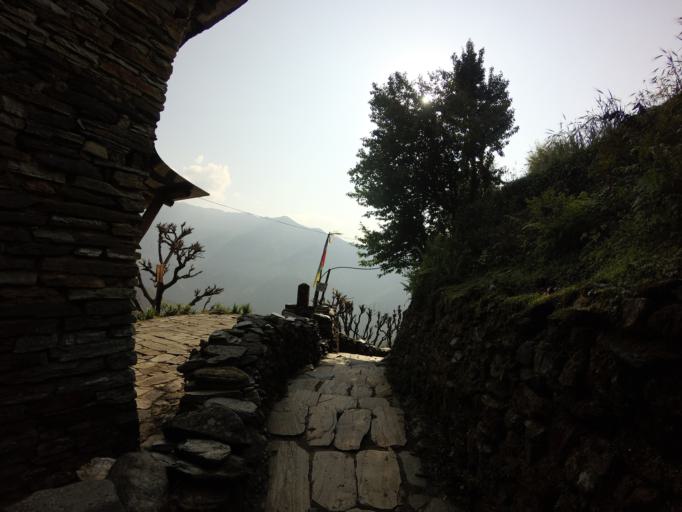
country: NP
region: Western Region
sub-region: Dhawalagiri Zone
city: Chitre
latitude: 28.3801
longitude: 83.8060
